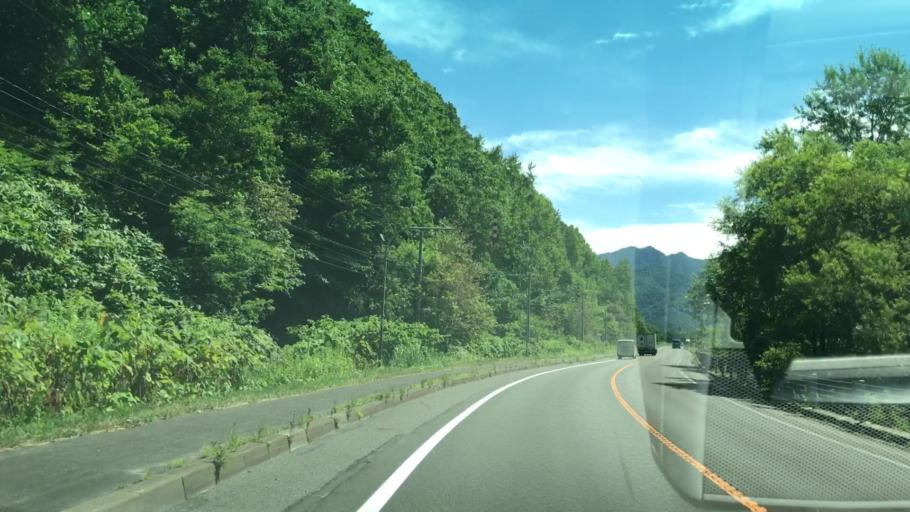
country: JP
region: Hokkaido
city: Shimo-furano
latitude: 42.8958
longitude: 142.4997
